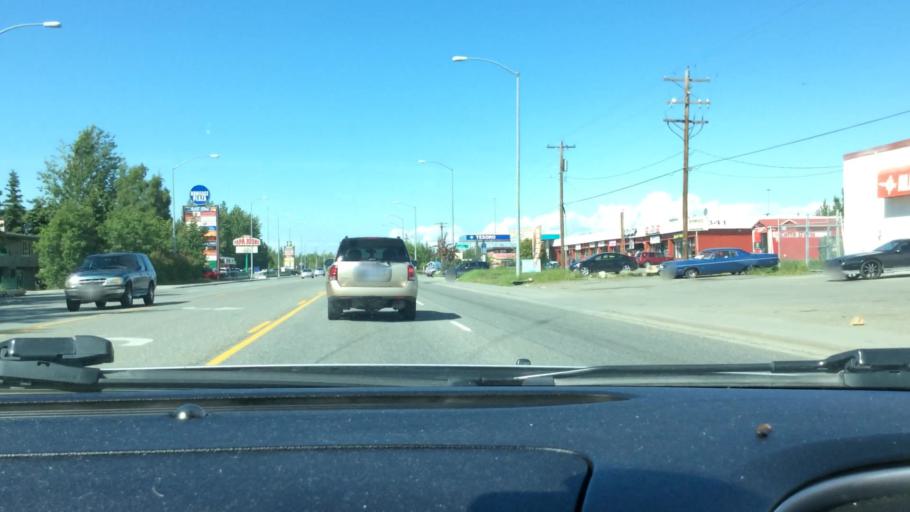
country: US
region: Alaska
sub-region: Anchorage Municipality
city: Anchorage
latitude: 61.2198
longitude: -149.7785
